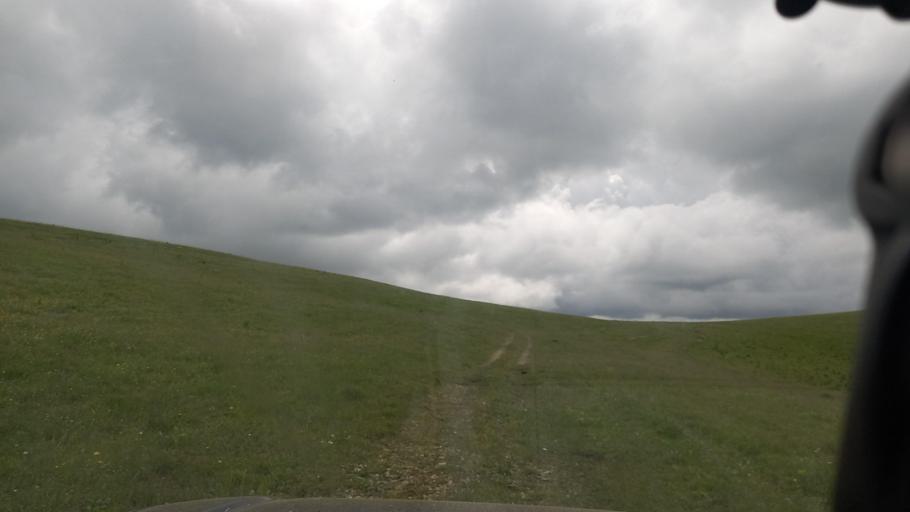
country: RU
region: Karachayevo-Cherkesiya
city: Pregradnaya
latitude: 43.9915
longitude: 41.2852
